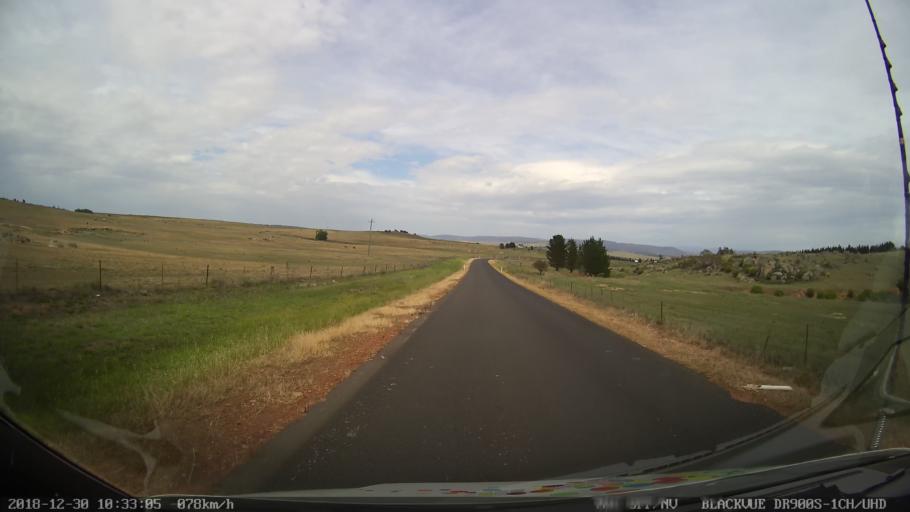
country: AU
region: New South Wales
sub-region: Snowy River
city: Berridale
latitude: -36.4988
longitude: 148.8575
